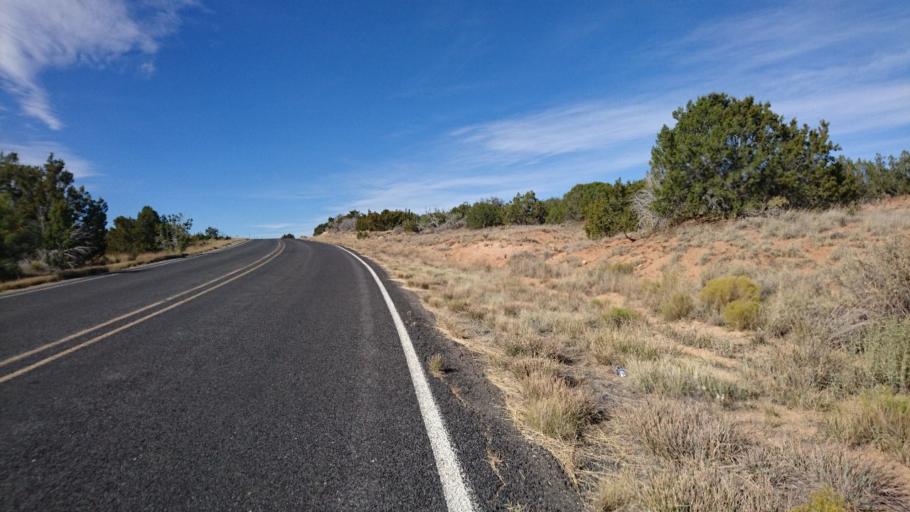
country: US
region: New Mexico
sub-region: Cibola County
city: Laguna
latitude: 35.0406
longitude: -107.3611
